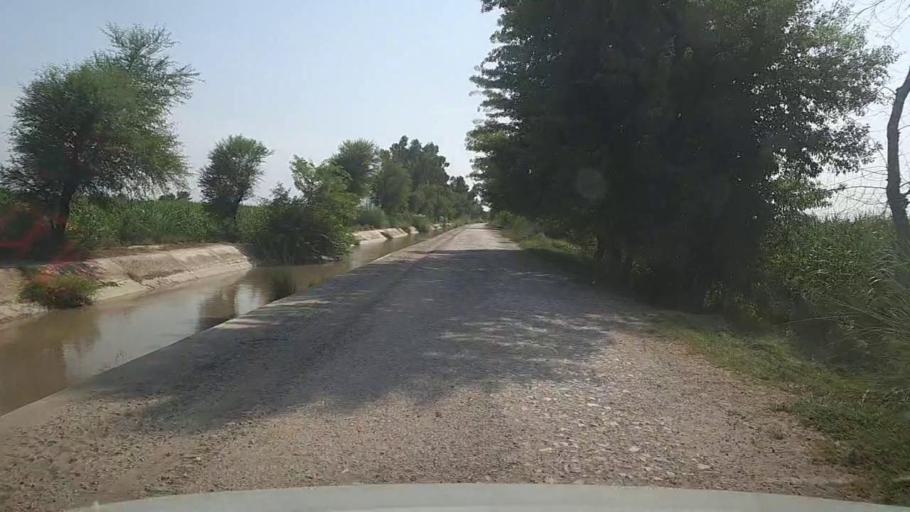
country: PK
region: Sindh
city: Mirpur Mathelo
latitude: 28.1203
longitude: 69.5969
